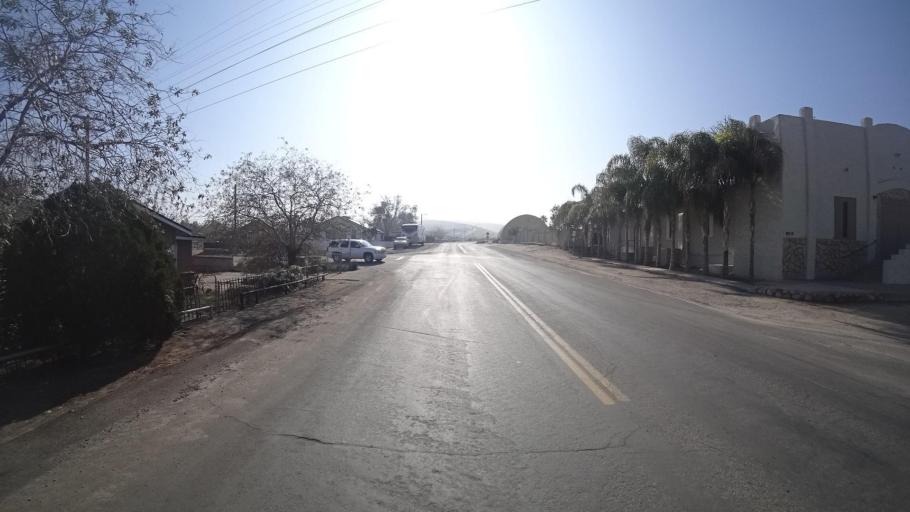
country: US
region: California
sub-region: Kern County
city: Taft Heights
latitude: 35.1333
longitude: -119.4649
